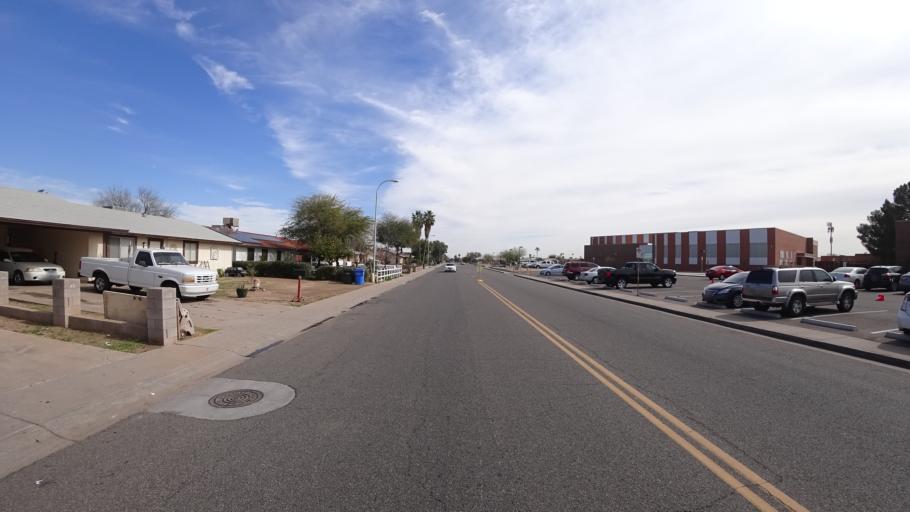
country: US
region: Arizona
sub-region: Maricopa County
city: Tolleson
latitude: 33.4871
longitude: -112.2447
